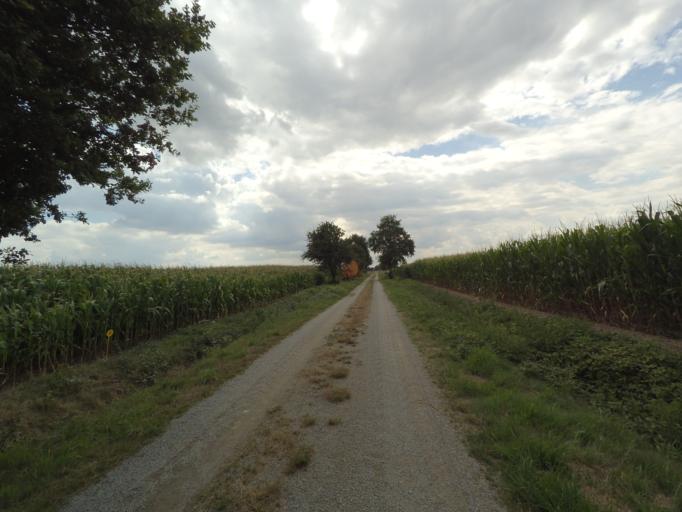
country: FR
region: Pays de la Loire
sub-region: Departement de la Loire-Atlantique
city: Vieillevigne
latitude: 46.9823
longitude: -1.4122
